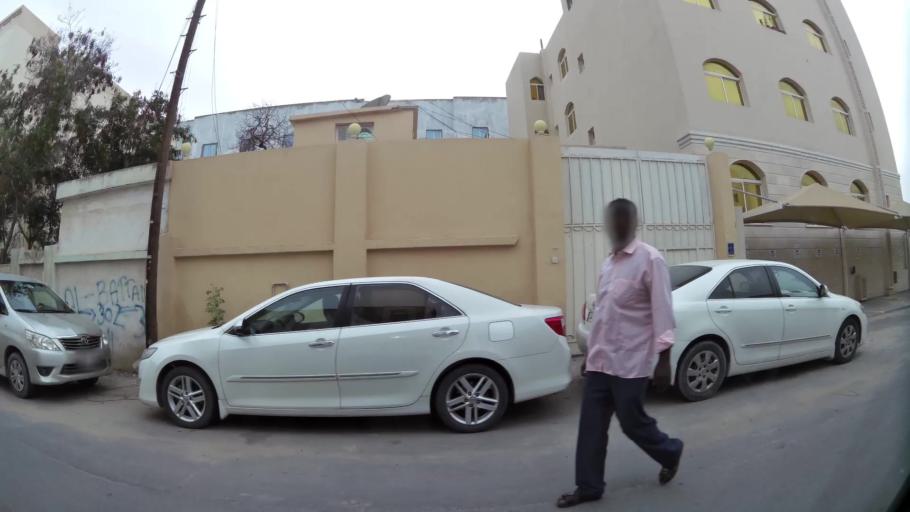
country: QA
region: Baladiyat ad Dawhah
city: Doha
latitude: 25.3048
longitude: 51.4941
